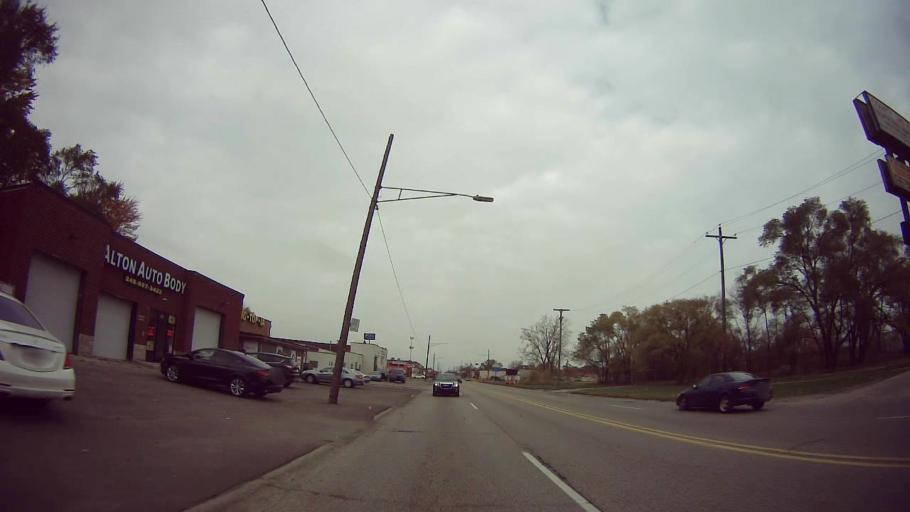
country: US
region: Michigan
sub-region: Oakland County
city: Hazel Park
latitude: 42.4498
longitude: -83.0836
